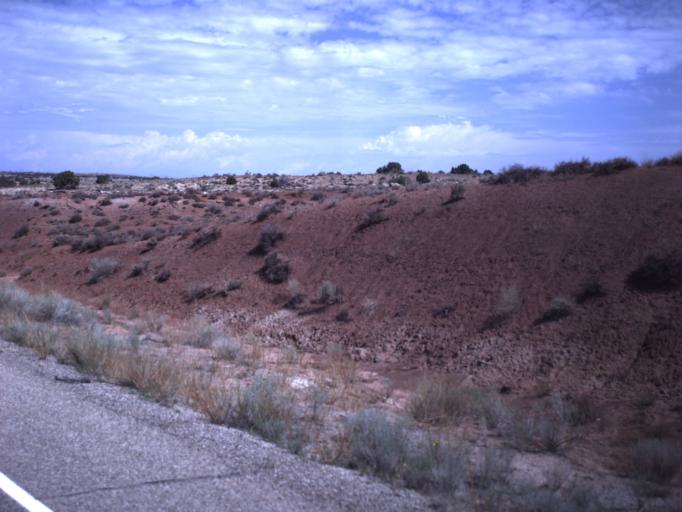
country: US
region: Utah
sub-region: Uintah County
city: Naples
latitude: 40.1631
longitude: -109.3121
